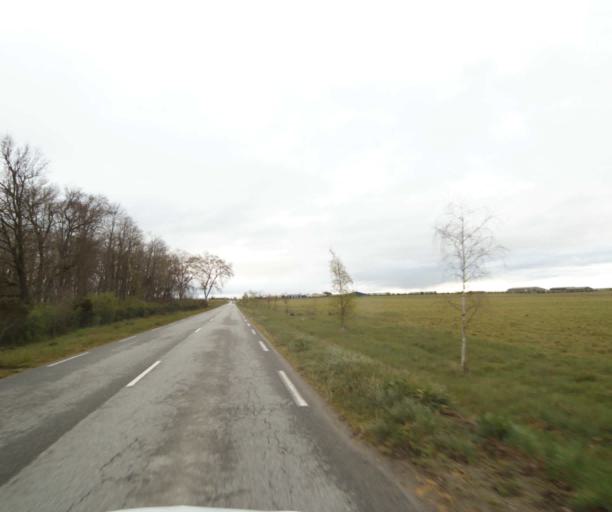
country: FR
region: Midi-Pyrenees
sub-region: Departement de l'Ariege
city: Saverdun
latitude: 43.2320
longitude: 1.6254
